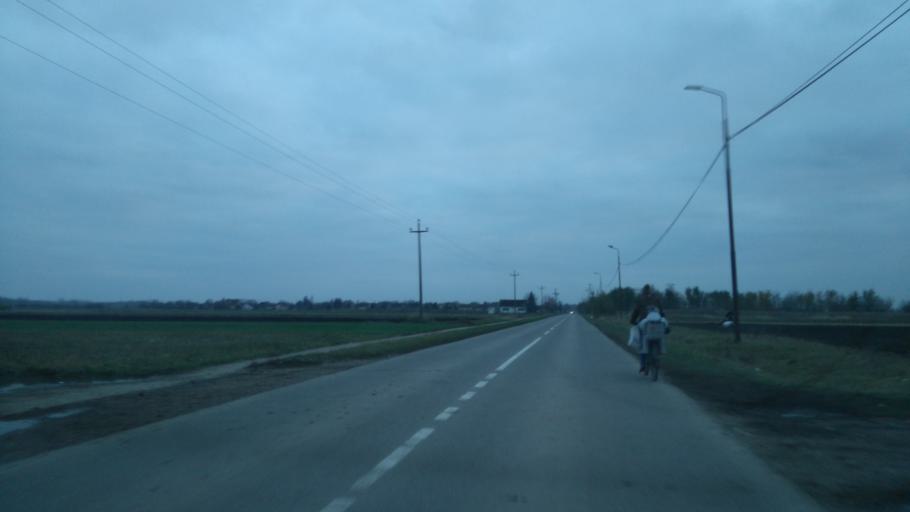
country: RS
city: Mol
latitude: 45.7810
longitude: 20.1279
